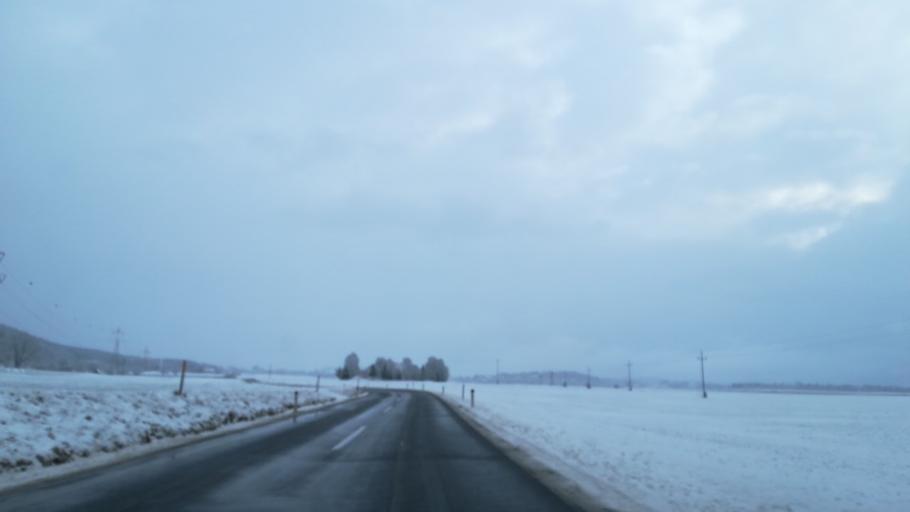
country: AT
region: Styria
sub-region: Politischer Bezirk Murtal
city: Fohnsdorf
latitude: 47.2061
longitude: 14.6351
